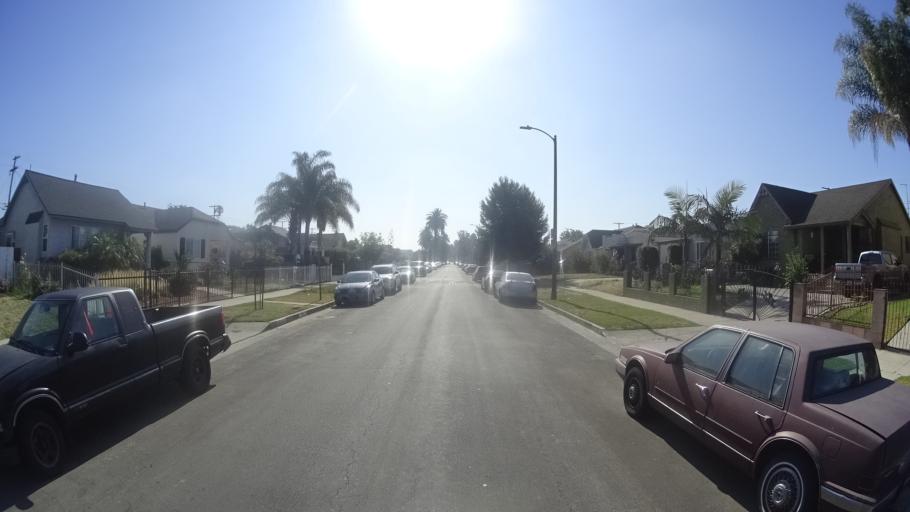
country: US
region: California
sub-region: Los Angeles County
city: Westmont
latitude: 33.9770
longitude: -118.2976
